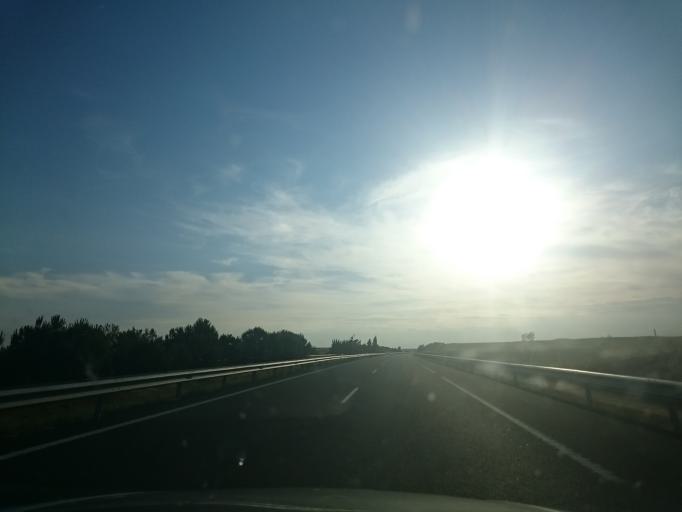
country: ES
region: Castille and Leon
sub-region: Provincia de Palencia
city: Moratinos
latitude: 42.3636
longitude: -4.9292
